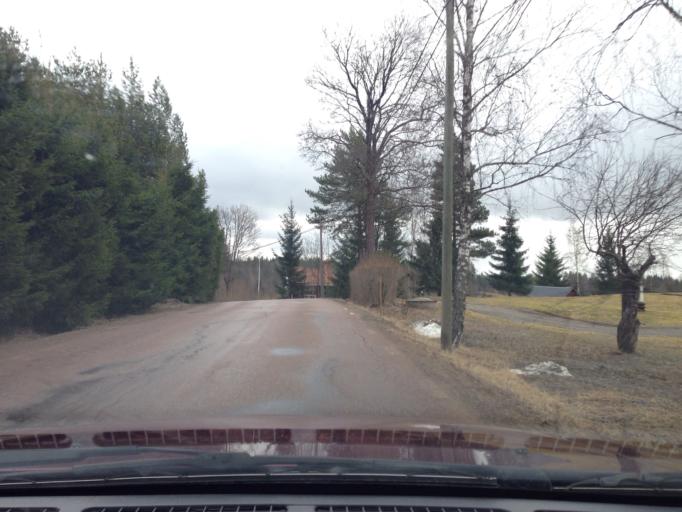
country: SE
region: Dalarna
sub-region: Smedjebackens Kommun
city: Smedjebacken
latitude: 60.1776
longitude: 15.3028
